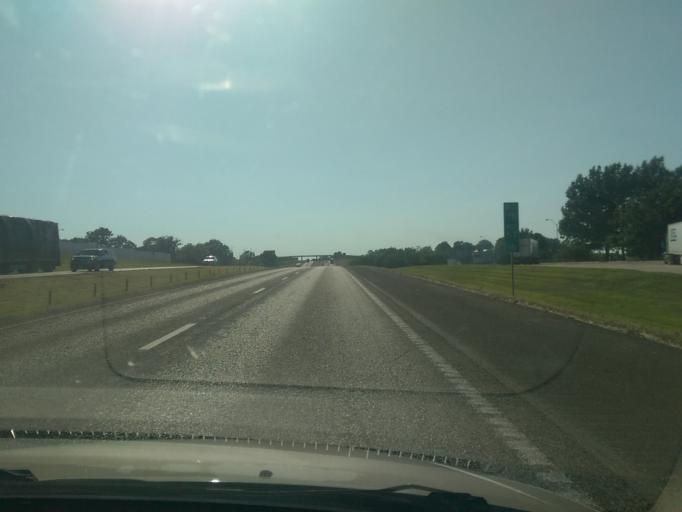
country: US
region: Missouri
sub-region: Lafayette County
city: Concordia
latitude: 38.9936
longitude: -93.5857
